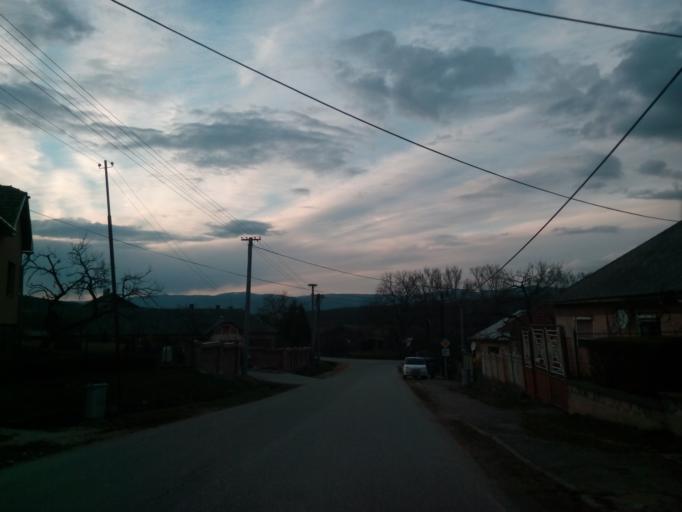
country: SK
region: Kosicky
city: Moldava nad Bodvou
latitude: 48.5589
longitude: 20.9603
